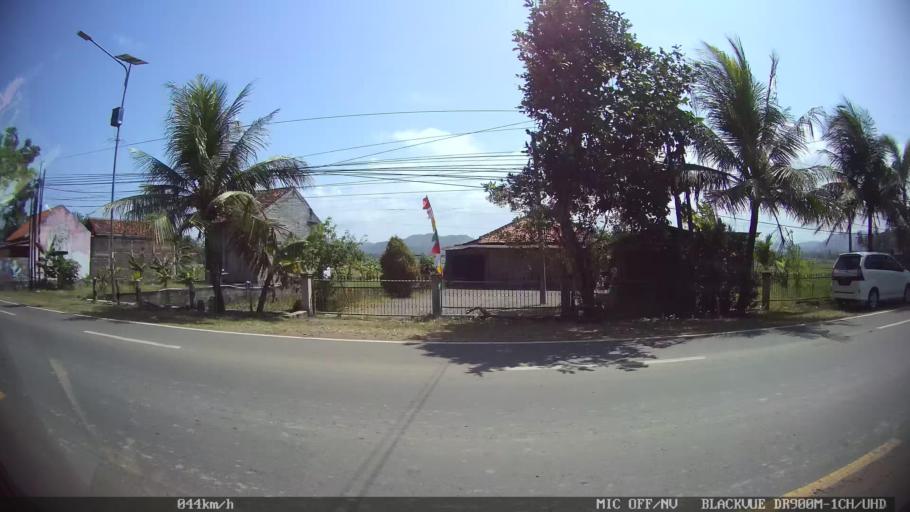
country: ID
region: Daerah Istimewa Yogyakarta
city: Srandakan
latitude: -7.8866
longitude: 110.0548
